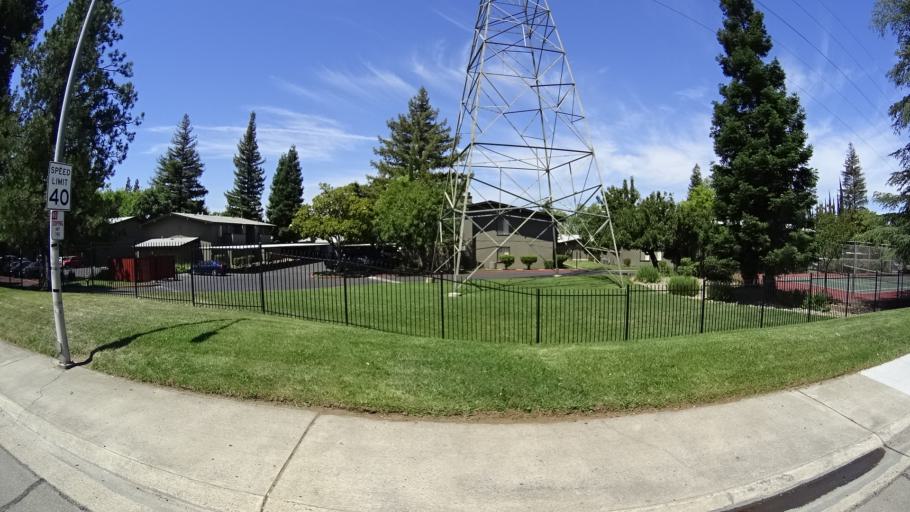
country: US
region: California
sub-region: Sacramento County
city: Arden-Arcade
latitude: 38.6064
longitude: -121.4155
